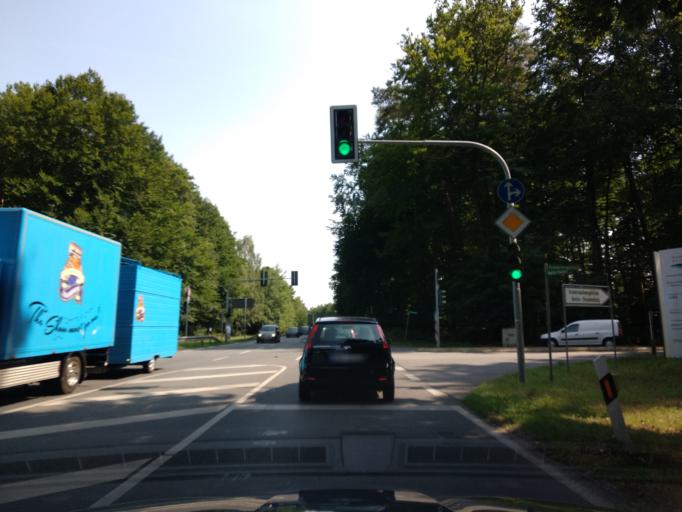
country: DE
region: Brandenburg
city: Wandlitz
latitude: 52.7328
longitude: 13.4960
